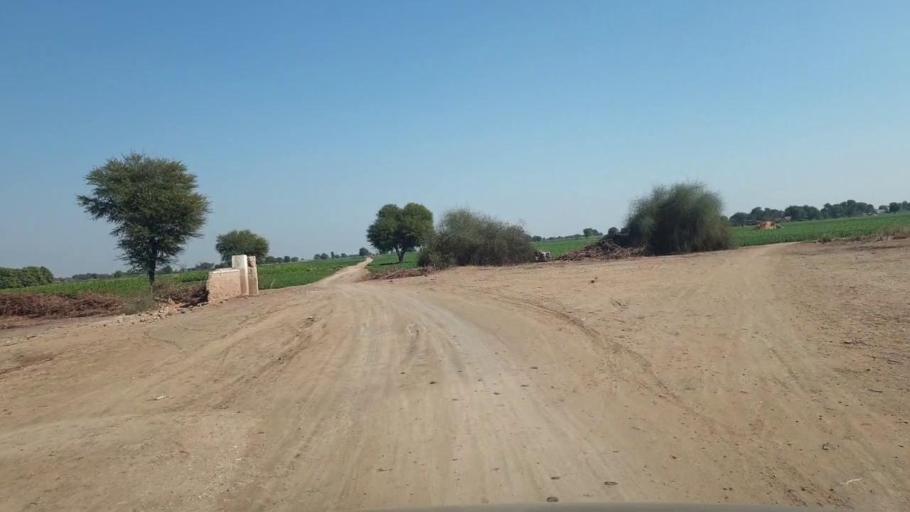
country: PK
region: Sindh
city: Shahpur Chakar
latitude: 26.1181
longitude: 68.6505
